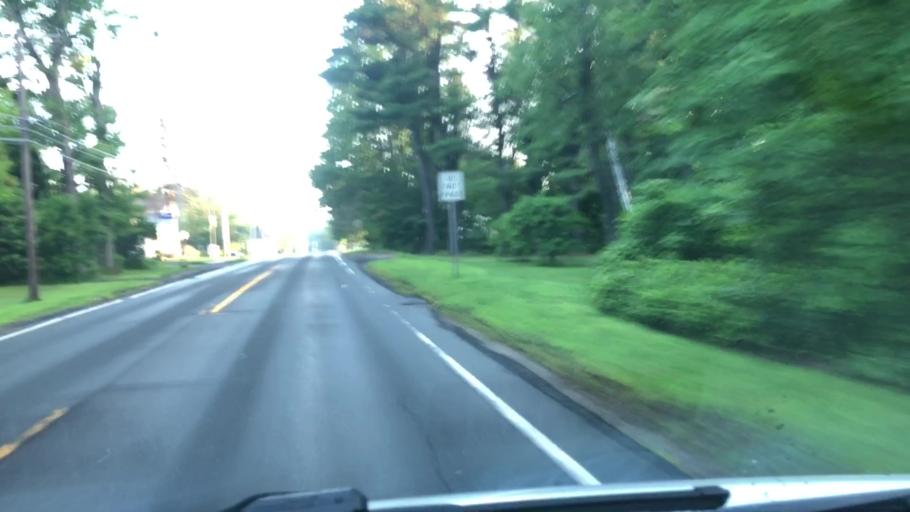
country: US
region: Massachusetts
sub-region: Hampshire County
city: Chesterfield
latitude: 42.4394
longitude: -72.7992
